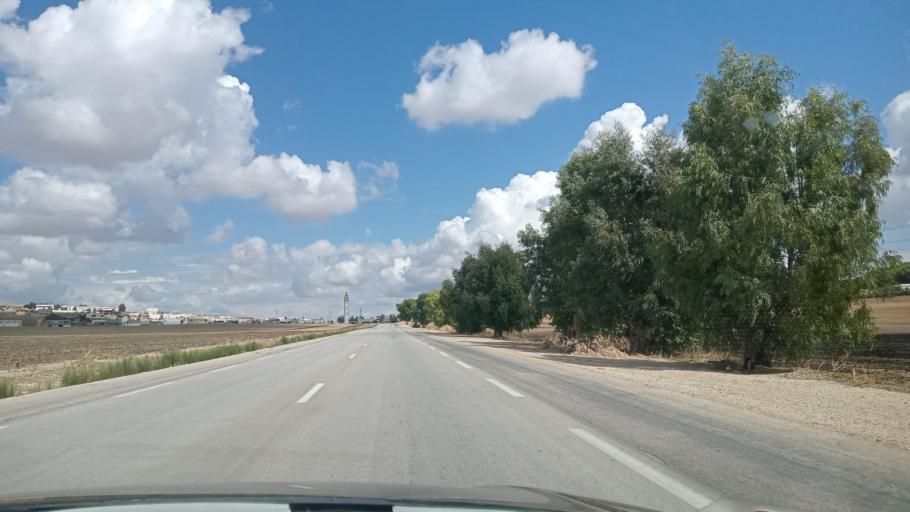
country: TN
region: Silyanah
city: Al Karib
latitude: 36.3208
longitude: 9.1242
